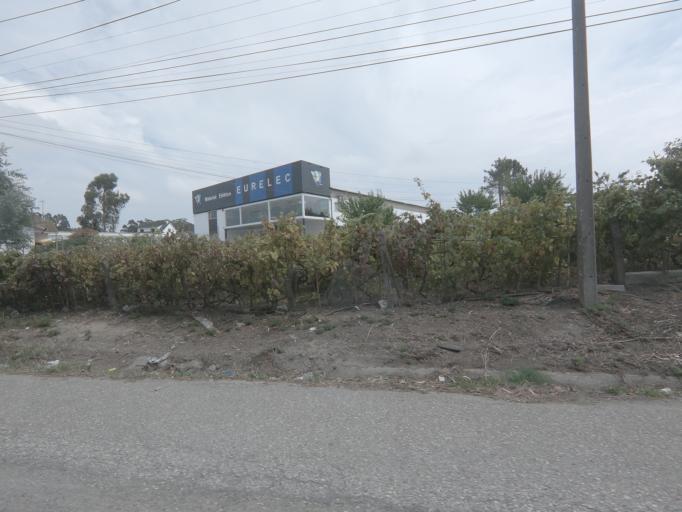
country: PT
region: Leiria
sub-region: Leiria
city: Leiria
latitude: 39.7752
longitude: -8.7636
